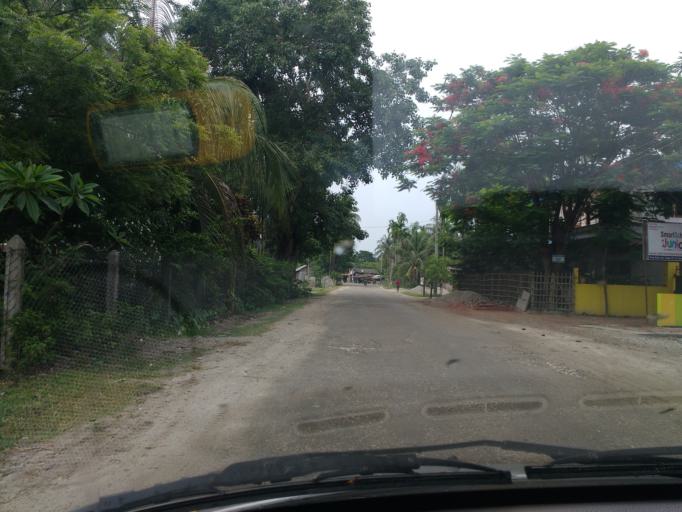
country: IN
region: Assam
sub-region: Udalguri
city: Udalguri
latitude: 26.7308
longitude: 92.2142
